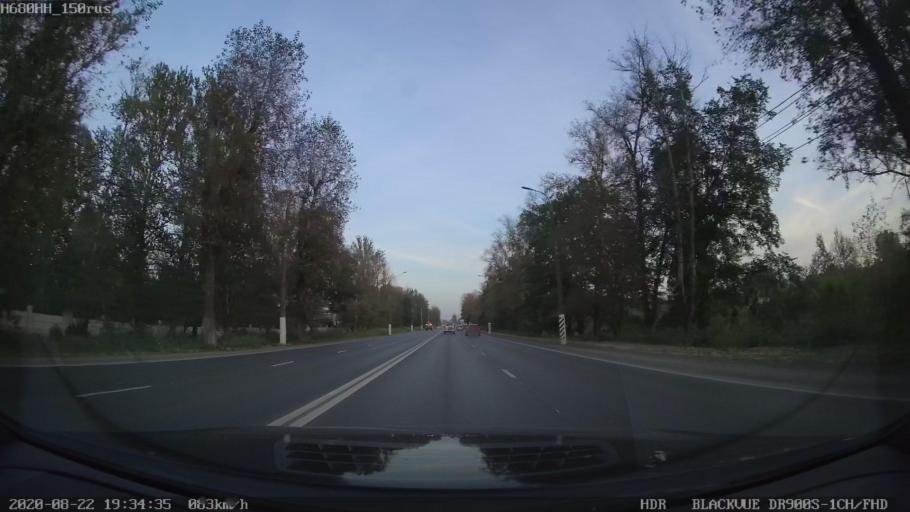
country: RU
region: Tverskaya
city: Tver
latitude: 56.8394
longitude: 35.9567
